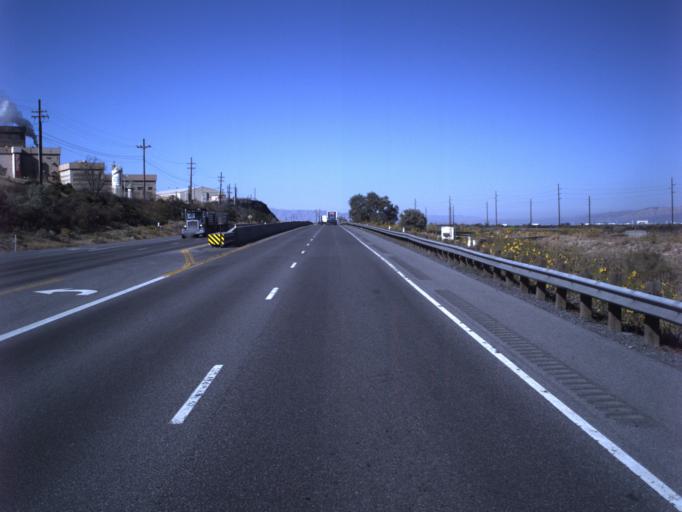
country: US
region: Utah
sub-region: Salt Lake County
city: Magna
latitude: 40.7276
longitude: -112.1874
